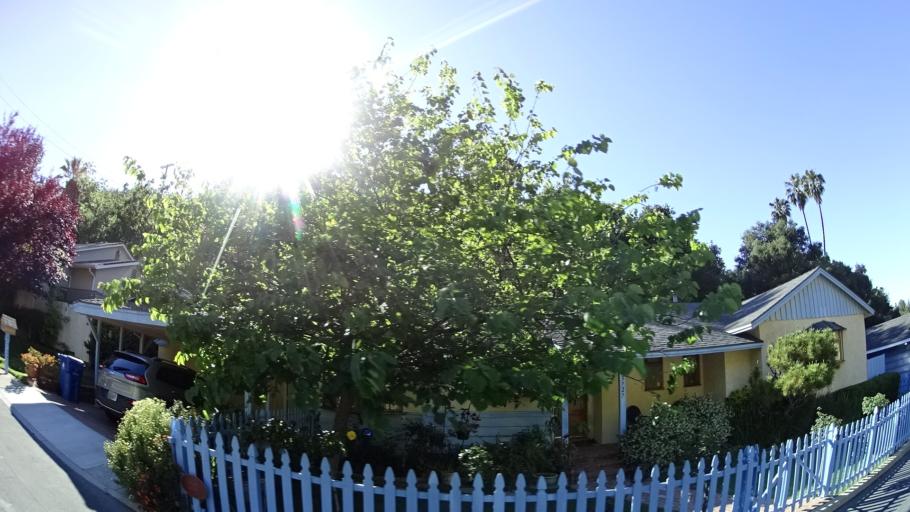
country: US
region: California
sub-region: Los Angeles County
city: Sherman Oaks
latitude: 34.1388
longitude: -118.4496
